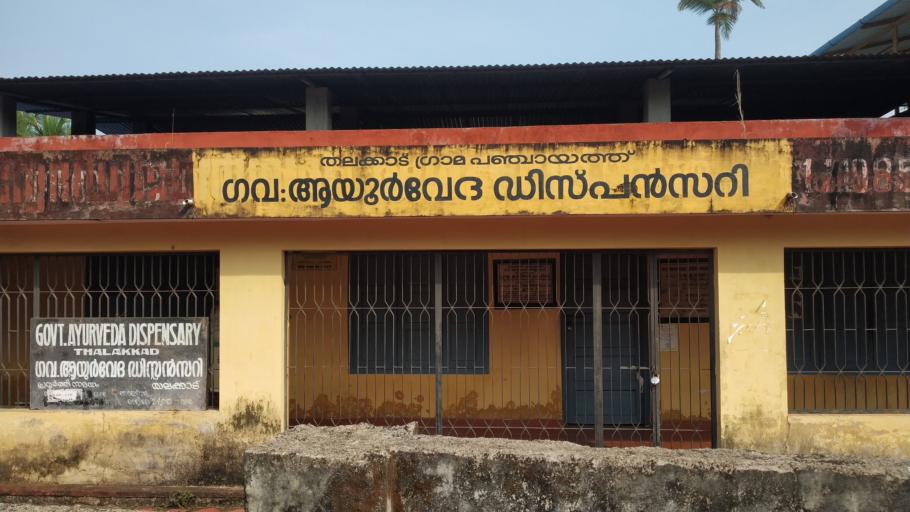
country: IN
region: Kerala
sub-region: Malappuram
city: Tirur
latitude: 10.8920
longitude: 75.9365
